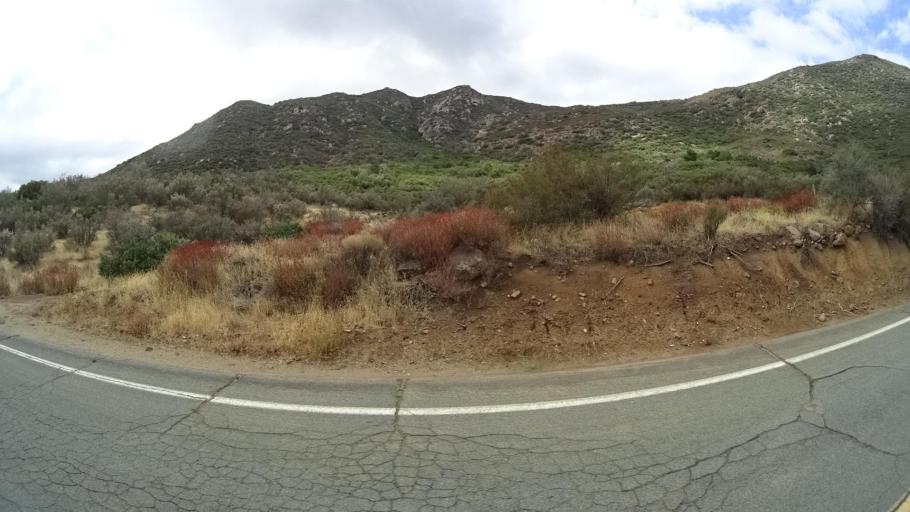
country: US
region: California
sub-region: San Diego County
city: Pine Valley
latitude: 32.7849
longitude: -116.4506
